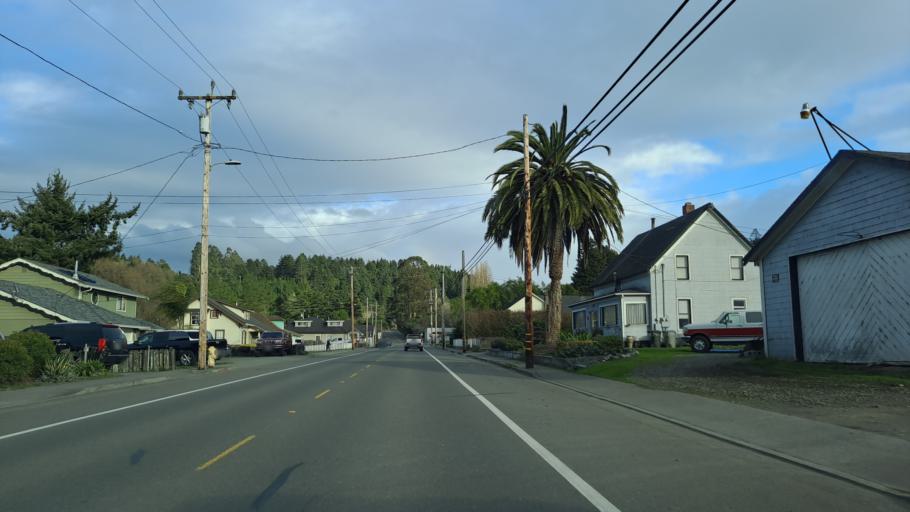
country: US
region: California
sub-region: Humboldt County
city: Hydesville
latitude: 40.5701
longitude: -124.1291
